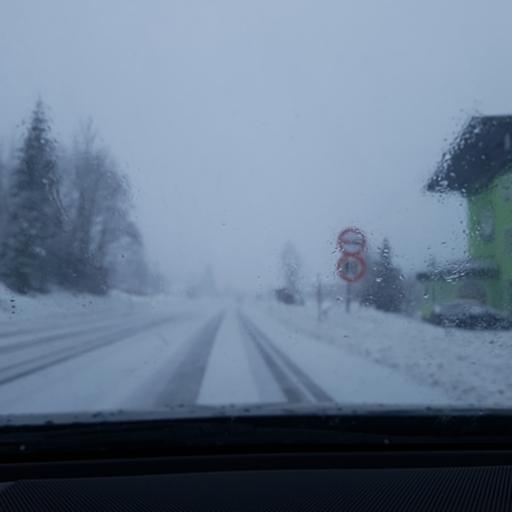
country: AT
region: Salzburg
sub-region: Politischer Bezirk Hallein
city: Abtenau
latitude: 47.5875
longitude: 13.4581
